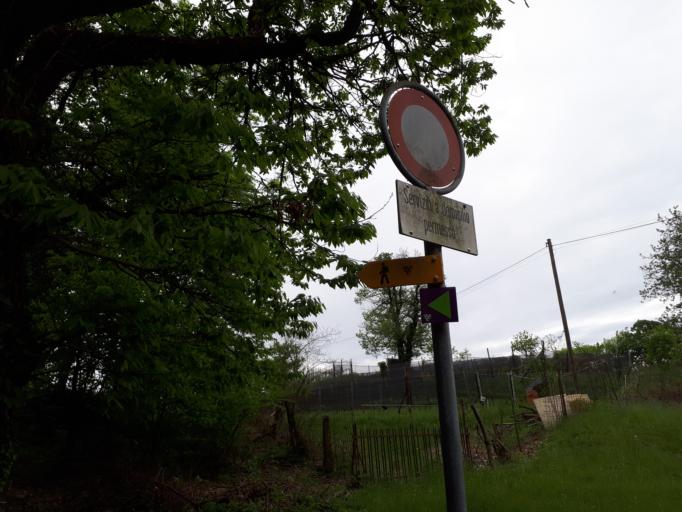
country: CH
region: Ticino
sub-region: Mendrisio District
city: Castel San Pietro
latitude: 45.8668
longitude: 9.0044
